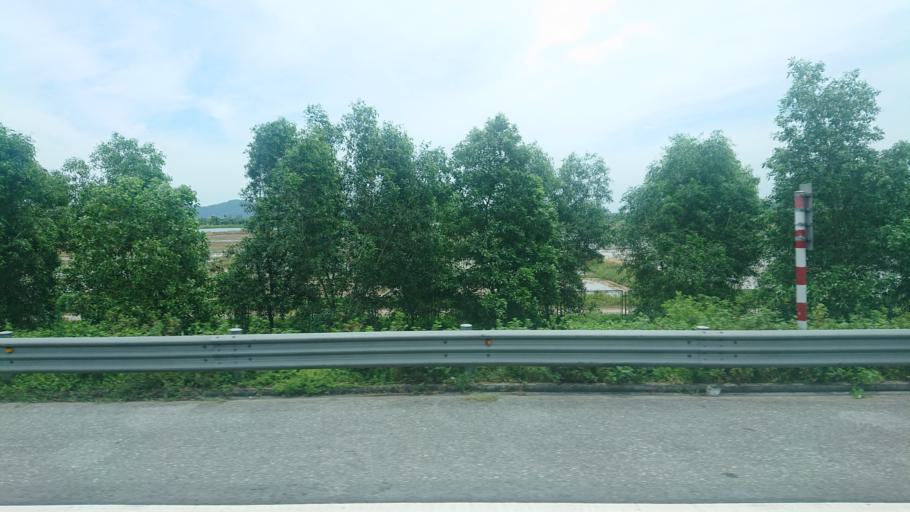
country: VN
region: Hai Phong
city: An Lao
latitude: 20.7783
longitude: 106.5733
